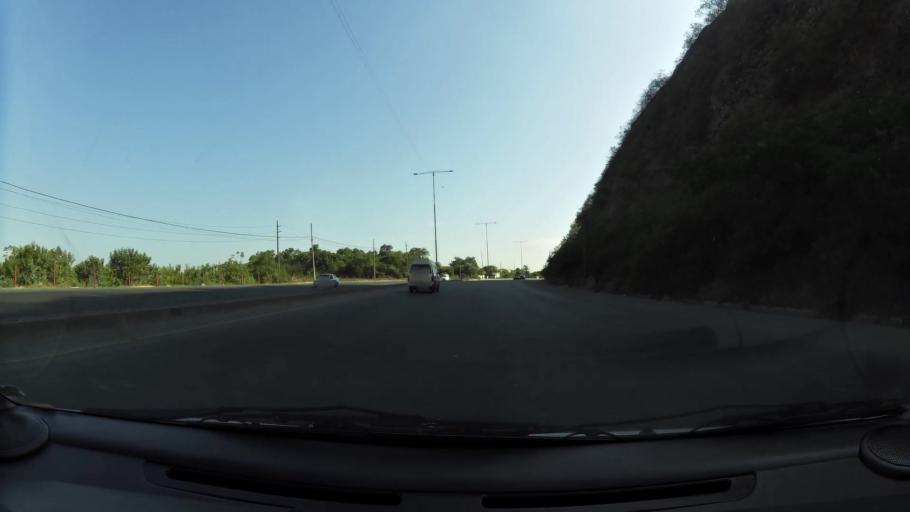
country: EC
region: Guayas
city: Guayaquil
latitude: -2.1841
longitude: -79.9495
